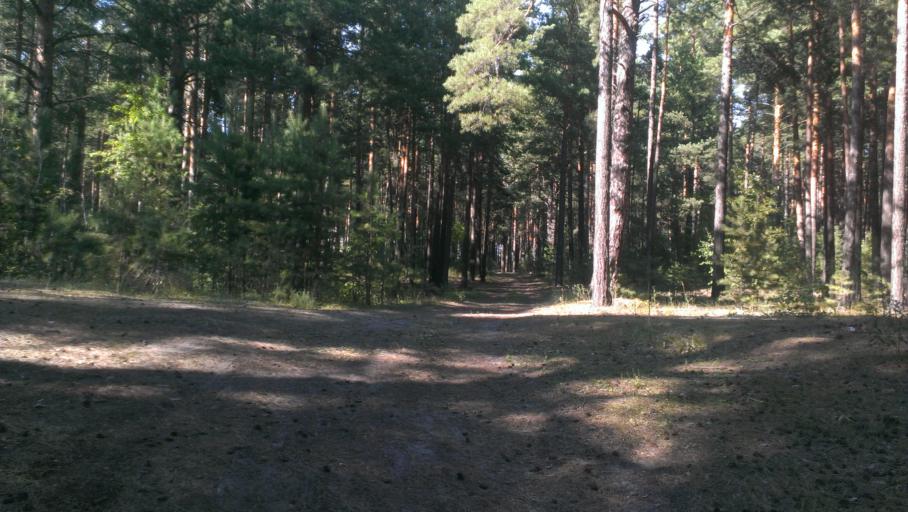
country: RU
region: Altai Krai
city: Novosilikatnyy
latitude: 53.3165
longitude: 83.6837
